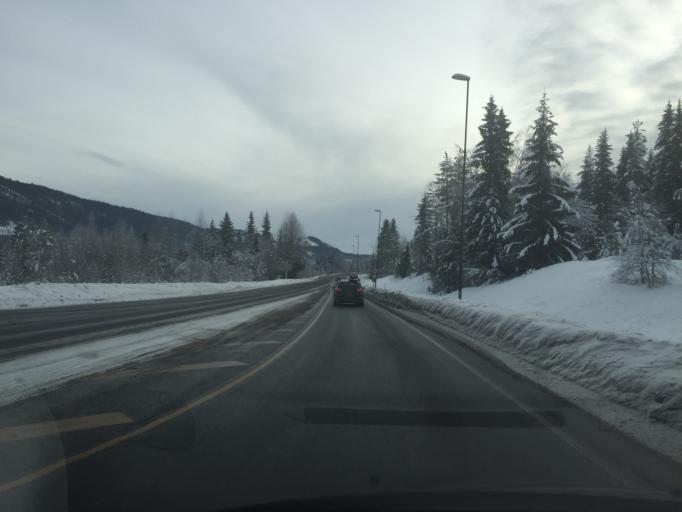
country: NO
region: Hedmark
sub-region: Trysil
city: Innbygda
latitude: 61.2711
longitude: 12.2982
